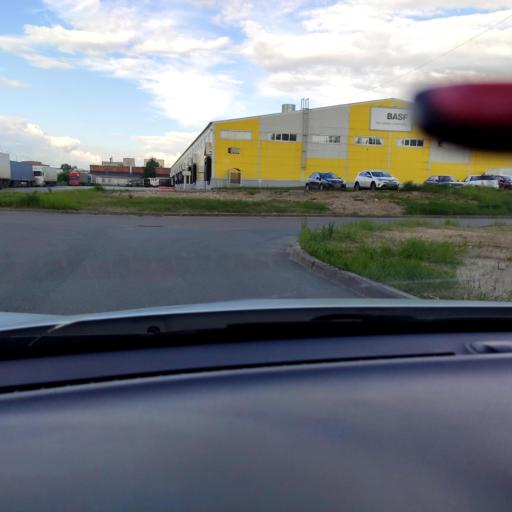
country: RU
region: Tatarstan
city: Staroye Arakchino
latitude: 55.8298
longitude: 49.0367
